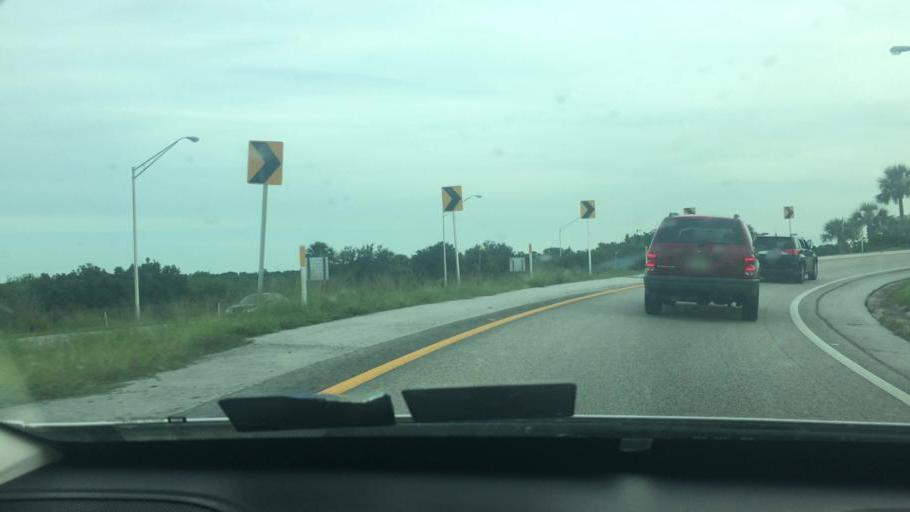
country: US
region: Florida
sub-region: Saint Lucie County
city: Fort Pierce South
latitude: 27.4150
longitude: -80.3866
